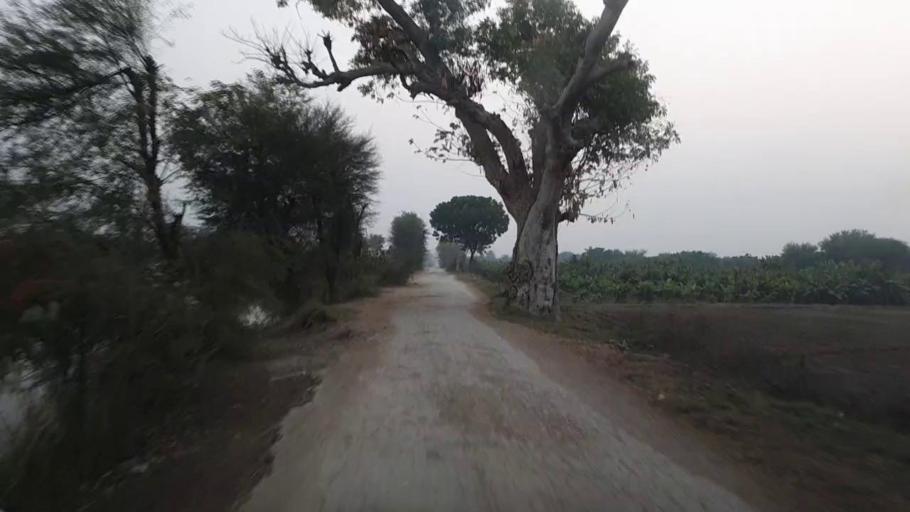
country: PK
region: Sindh
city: Karaundi
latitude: 26.9389
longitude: 68.4444
